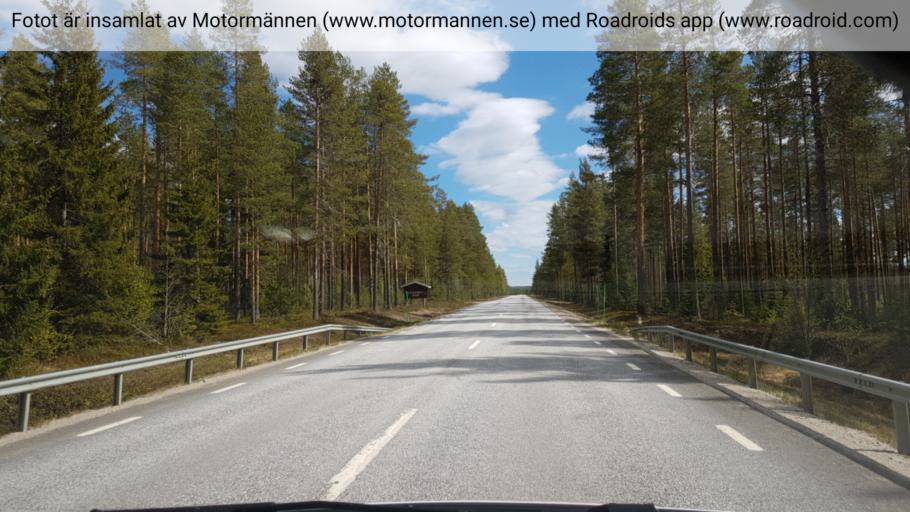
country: SE
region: Vaesterbotten
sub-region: Vindelns Kommun
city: Vindeln
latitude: 64.2136
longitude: 19.3958
